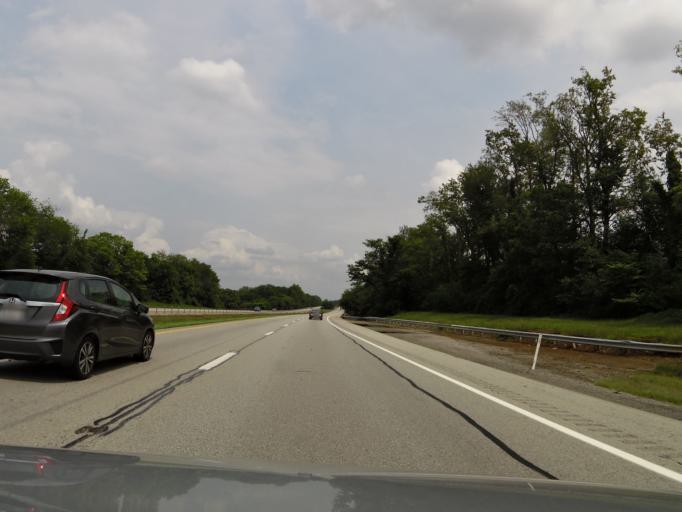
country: US
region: Kentucky
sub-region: Jefferson County
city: Worthington
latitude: 38.3172
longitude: -85.5755
